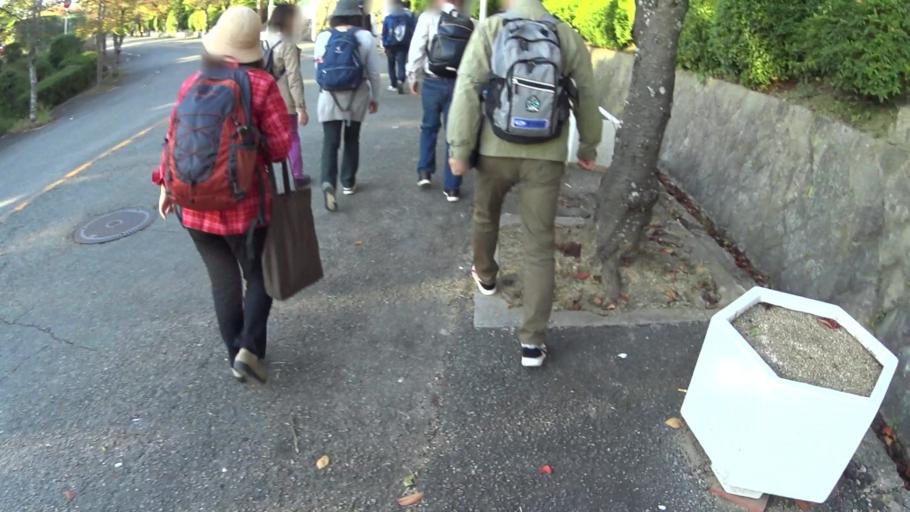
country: JP
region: Osaka
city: Ikeda
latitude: 34.8290
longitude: 135.4276
